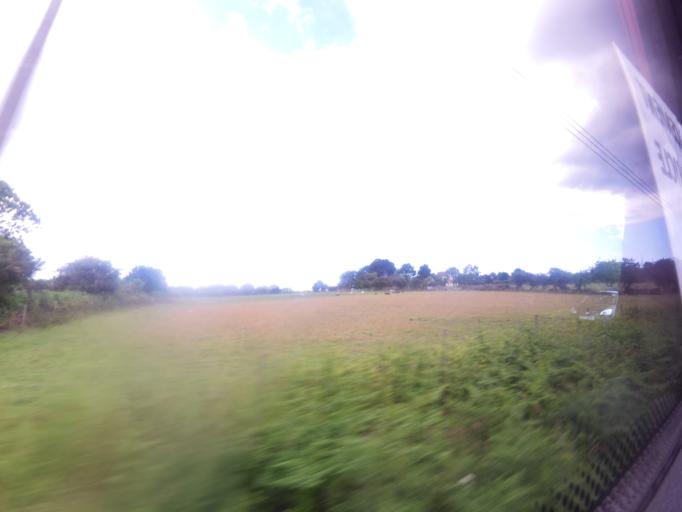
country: GB
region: England
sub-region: Norfolk
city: Cromer
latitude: 52.8904
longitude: 1.2987
